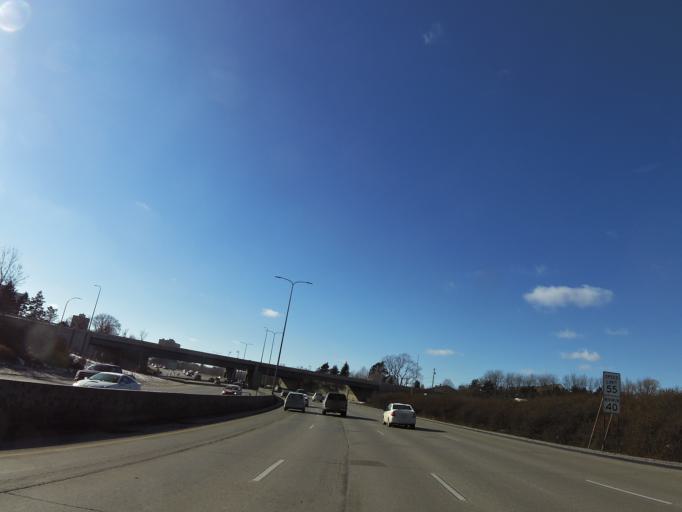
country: US
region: Minnesota
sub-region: Ramsey County
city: Lauderdale
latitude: 44.9673
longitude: -93.2215
